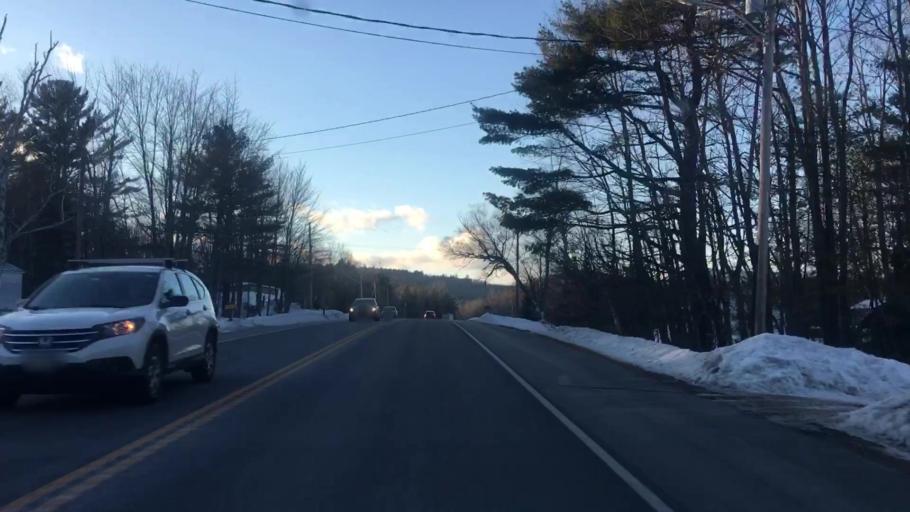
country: US
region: Maine
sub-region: Franklin County
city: Wilton
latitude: 44.5842
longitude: -70.2418
